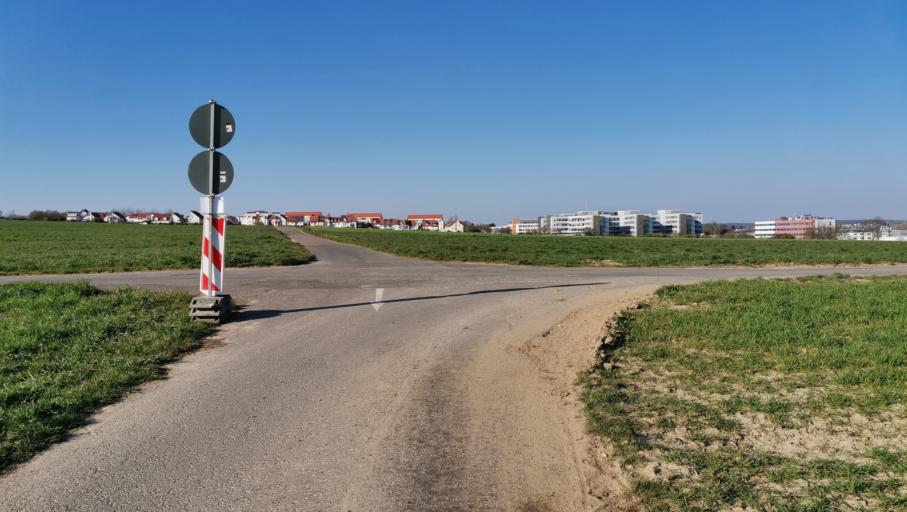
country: DE
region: Hesse
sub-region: Regierungsbezirk Darmstadt
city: Bad Vilbel
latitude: 50.1982
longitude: 8.7384
